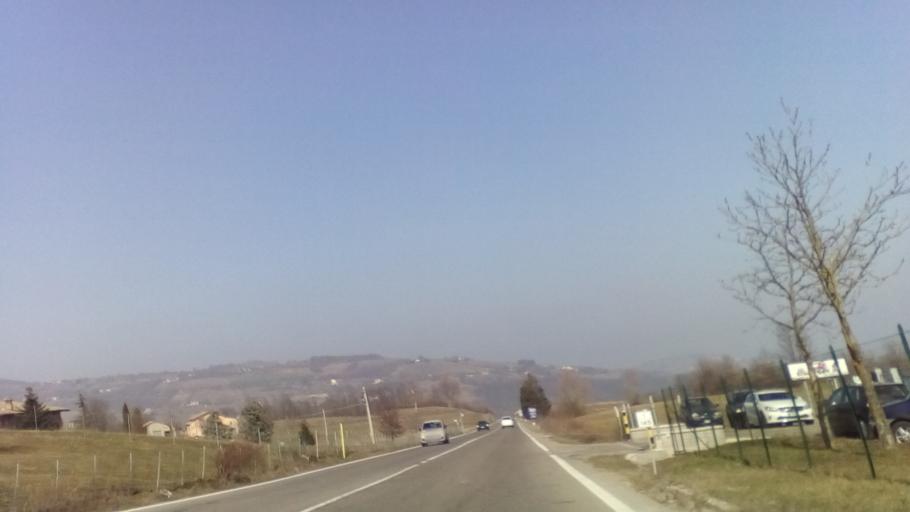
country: IT
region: Emilia-Romagna
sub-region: Provincia di Modena
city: Sant'Antonio
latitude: 44.3895
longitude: 10.8180
